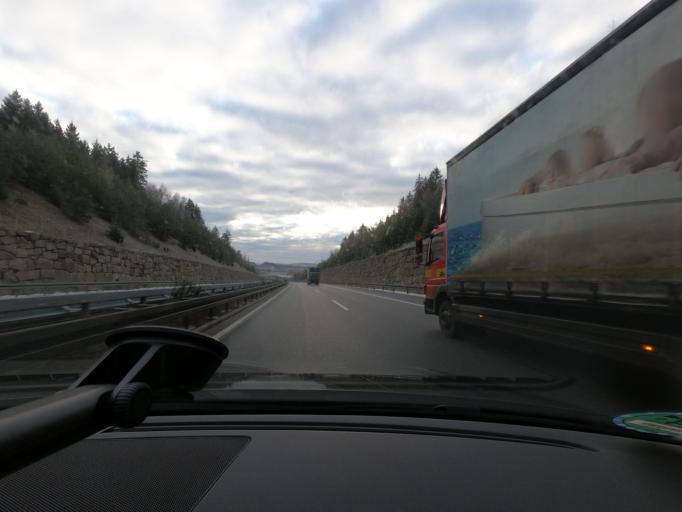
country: DE
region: Thuringia
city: Sankt Kilian
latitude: 50.5267
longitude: 10.7481
